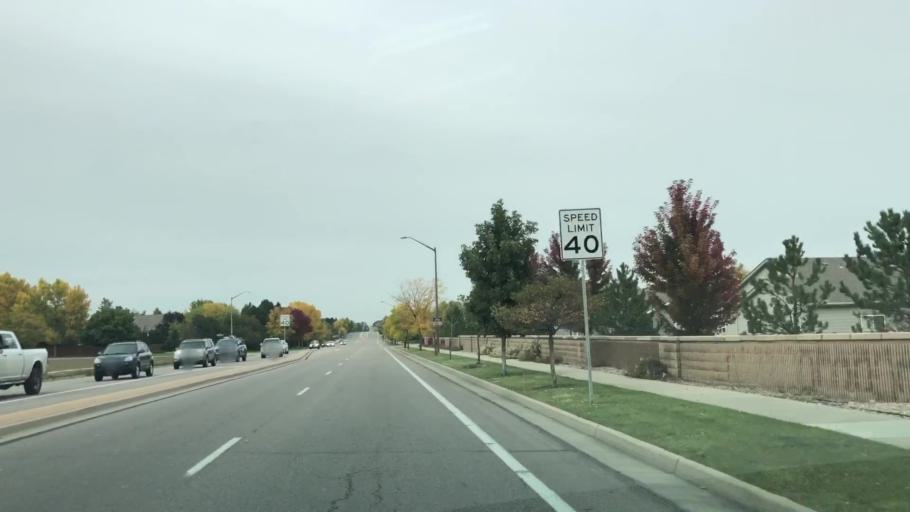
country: US
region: Colorado
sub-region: Larimer County
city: Fort Collins
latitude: 40.4947
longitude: -105.0581
